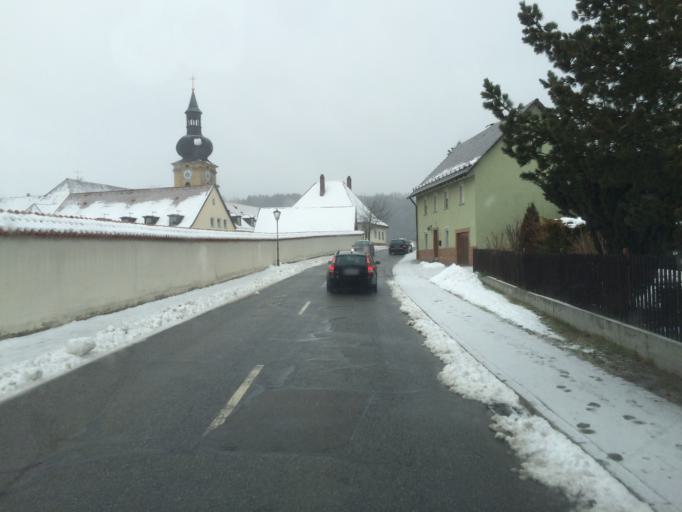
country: DE
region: Bavaria
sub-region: Upper Palatinate
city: Ensdorf
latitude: 49.3419
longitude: 11.9379
